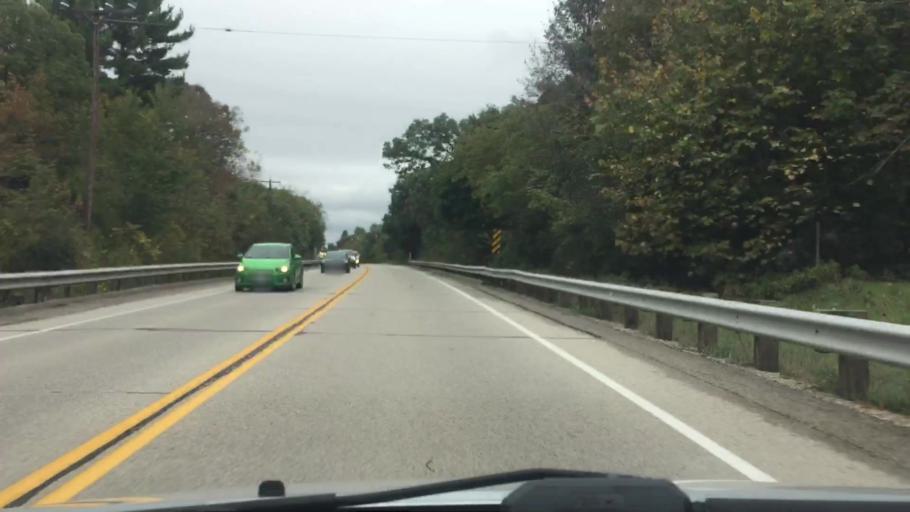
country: US
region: Wisconsin
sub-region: Jefferson County
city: Palmyra
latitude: 42.7860
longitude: -88.5609
